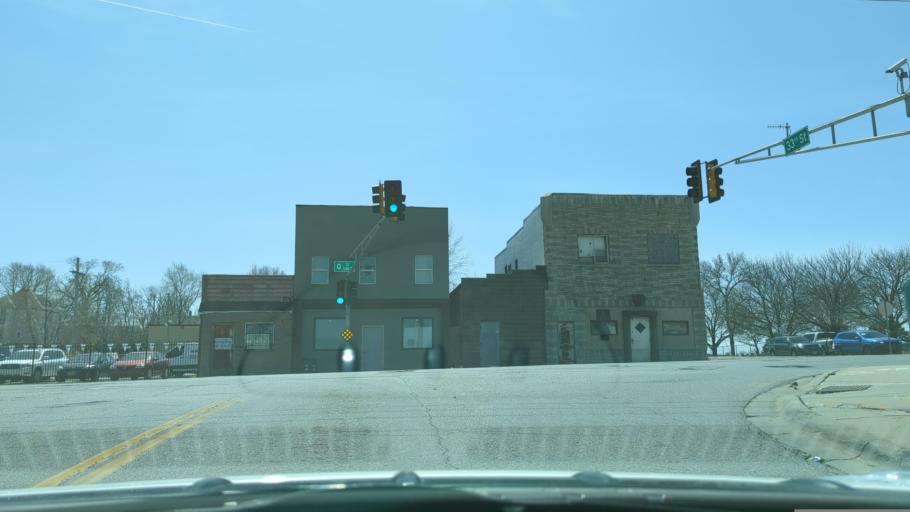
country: US
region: Nebraska
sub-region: Douglas County
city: Omaha
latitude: 41.2057
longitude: -95.9629
